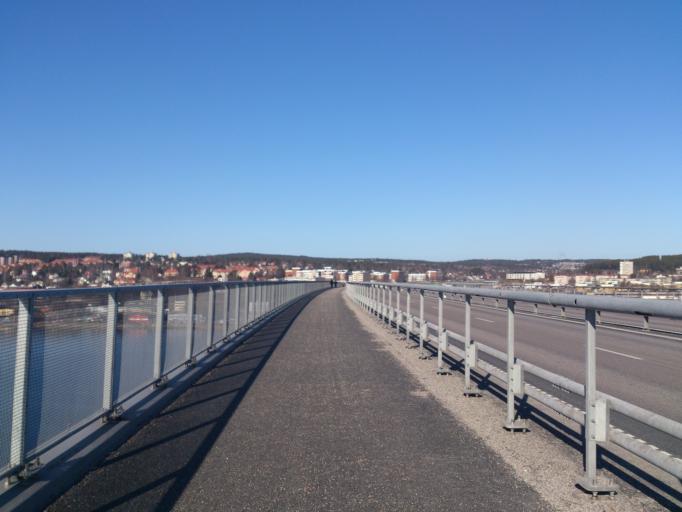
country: SE
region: Vaesternorrland
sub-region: Sundsvalls Kommun
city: Sundsvall
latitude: 62.3888
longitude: 17.3409
